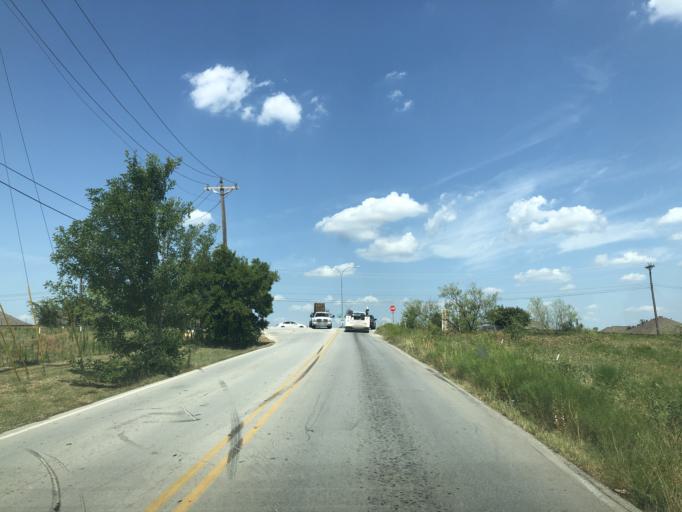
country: US
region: Texas
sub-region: Tarrant County
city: Haslet
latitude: 32.9241
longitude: -97.3324
